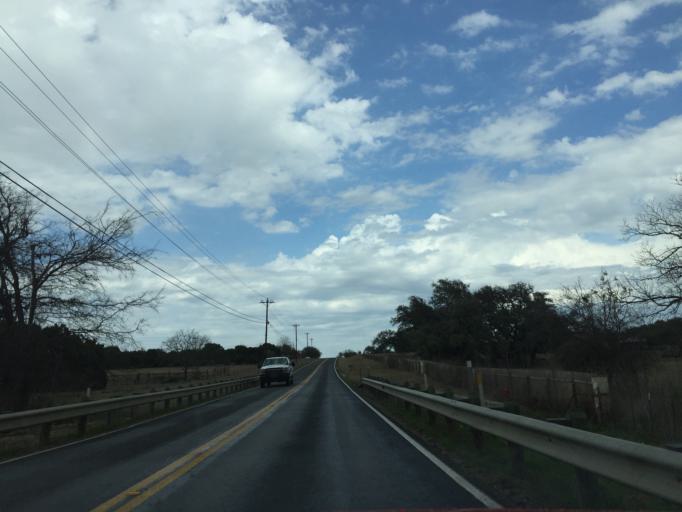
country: US
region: Texas
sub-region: Burnet County
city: Bertram
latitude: 30.7002
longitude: -97.9310
